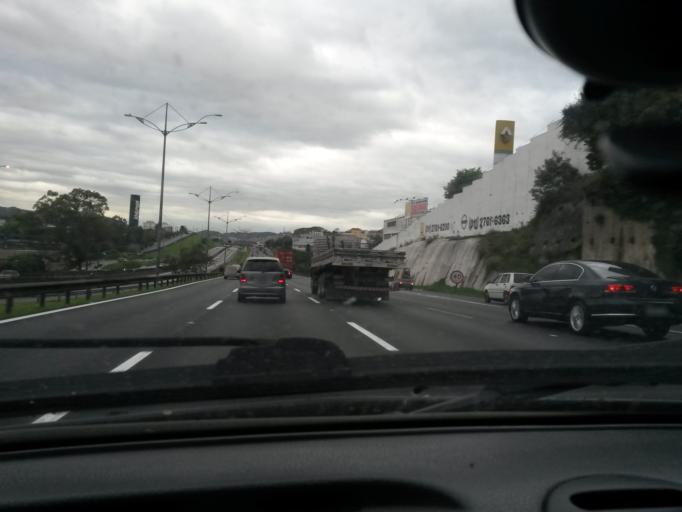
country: BR
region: Sao Paulo
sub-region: Sao Bernardo Do Campo
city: Sao Bernardo do Campo
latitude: -23.7166
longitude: -46.5602
